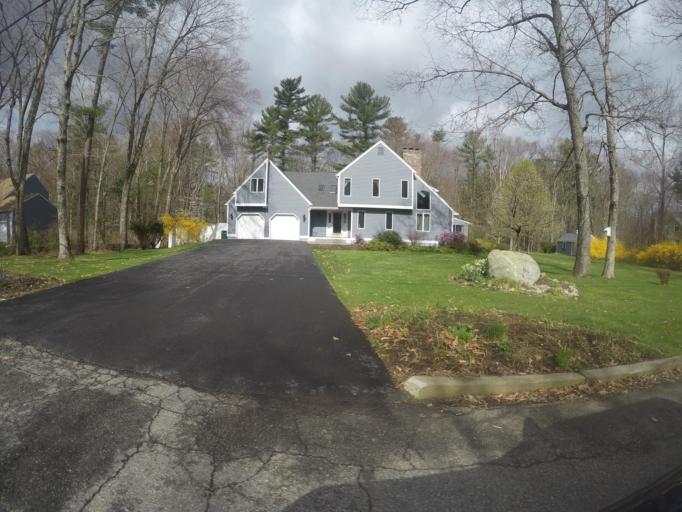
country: US
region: Massachusetts
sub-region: Bristol County
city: Easton
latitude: 42.0345
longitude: -71.1292
